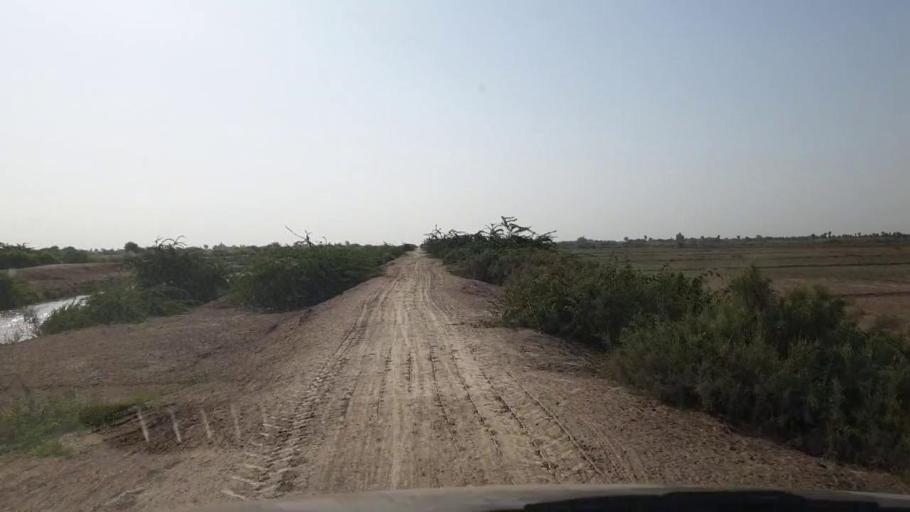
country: PK
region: Sindh
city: Kadhan
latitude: 24.5835
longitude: 69.0788
